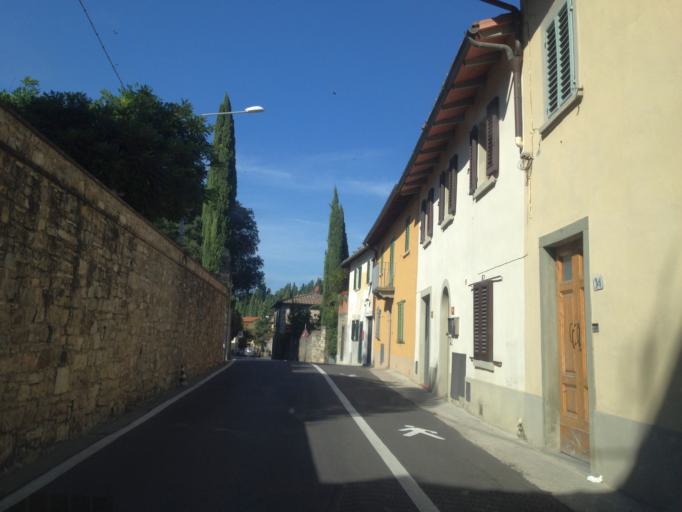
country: IT
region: Tuscany
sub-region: Province of Florence
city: Panzano in Chianti
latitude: 43.5452
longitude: 11.3150
